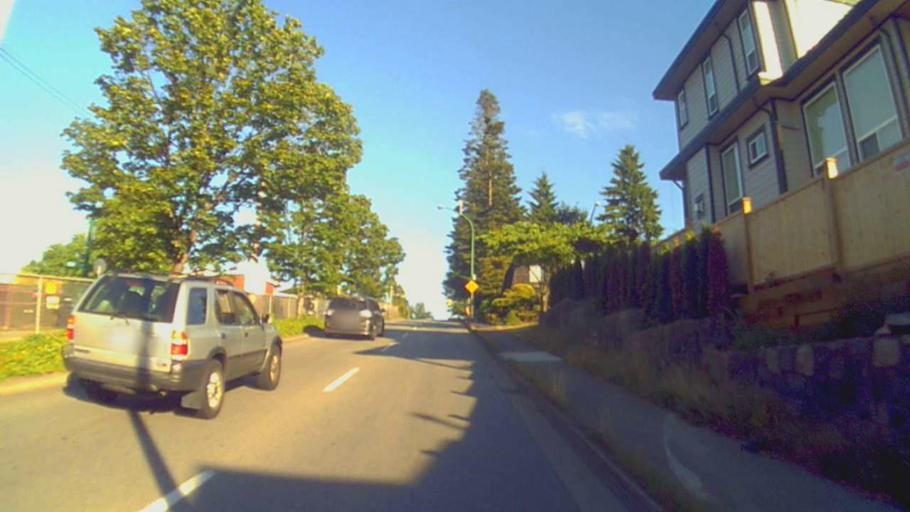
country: CA
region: British Columbia
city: New Westminster
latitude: 49.2359
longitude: -122.9048
